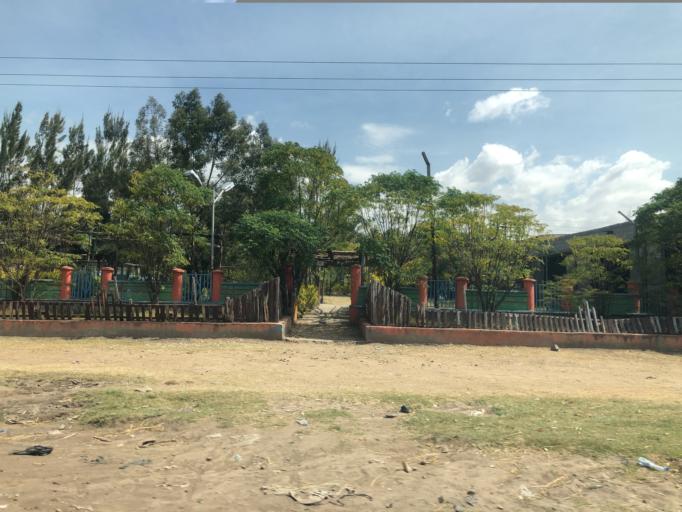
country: ET
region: Oromiya
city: Shashemene
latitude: 7.3123
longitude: 38.6516
